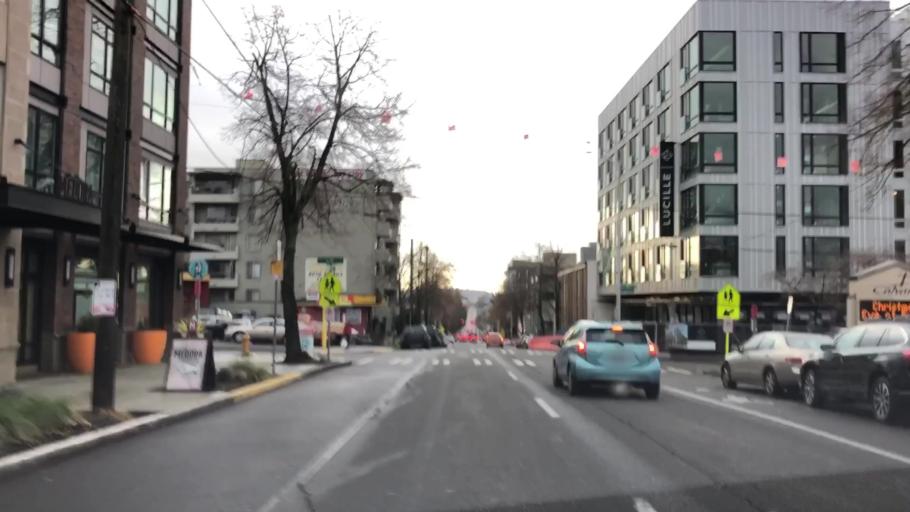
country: US
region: Washington
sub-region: King County
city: Seattle
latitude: 47.6784
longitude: -122.3174
